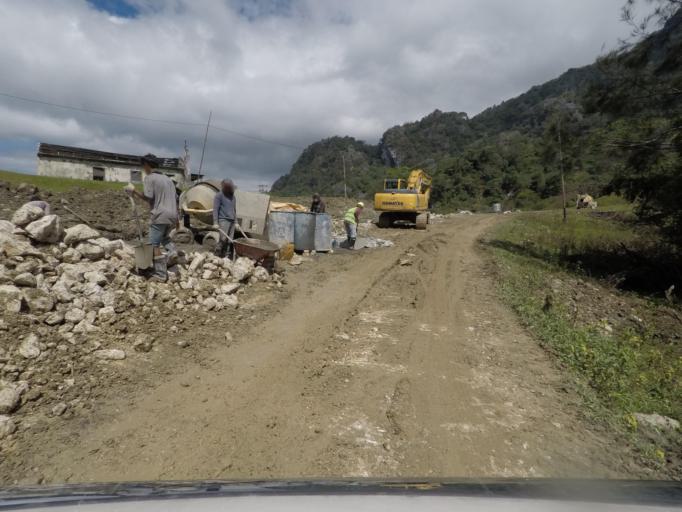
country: TL
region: Baucau
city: Venilale
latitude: -8.7264
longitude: 126.3688
